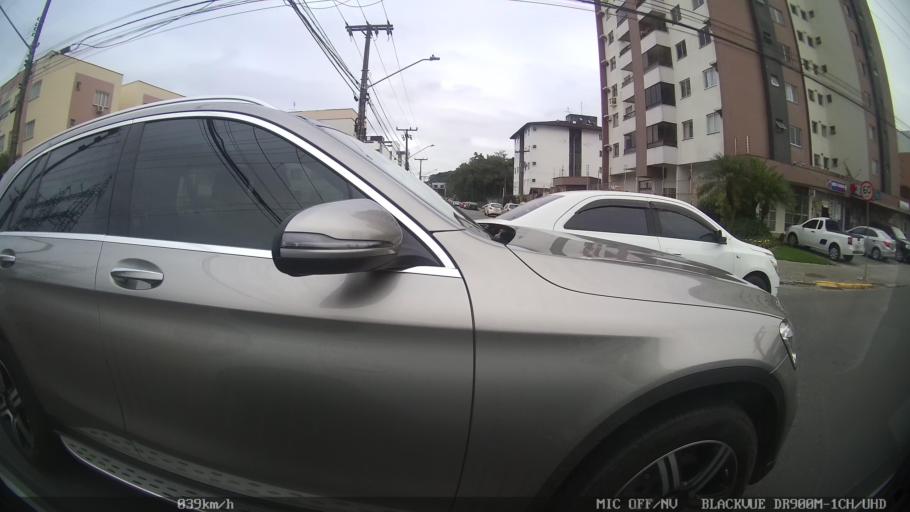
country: BR
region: Santa Catarina
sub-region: Joinville
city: Joinville
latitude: -26.2936
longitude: -48.8658
